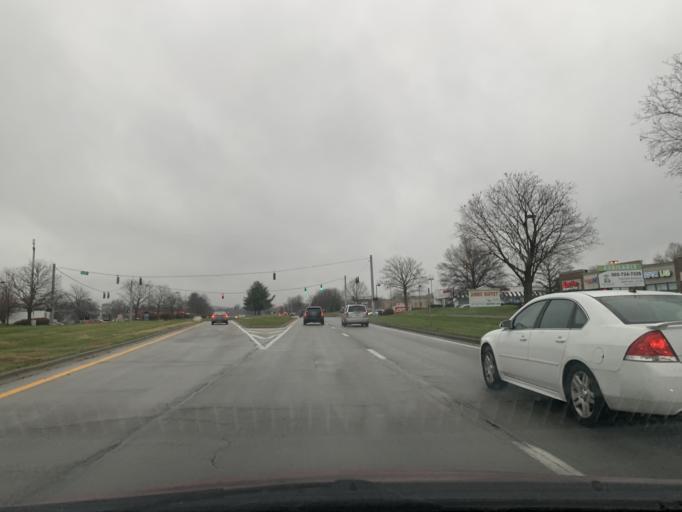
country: US
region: Kentucky
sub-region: Jefferson County
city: Hurstbourne Acres
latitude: 38.2114
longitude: -85.5965
